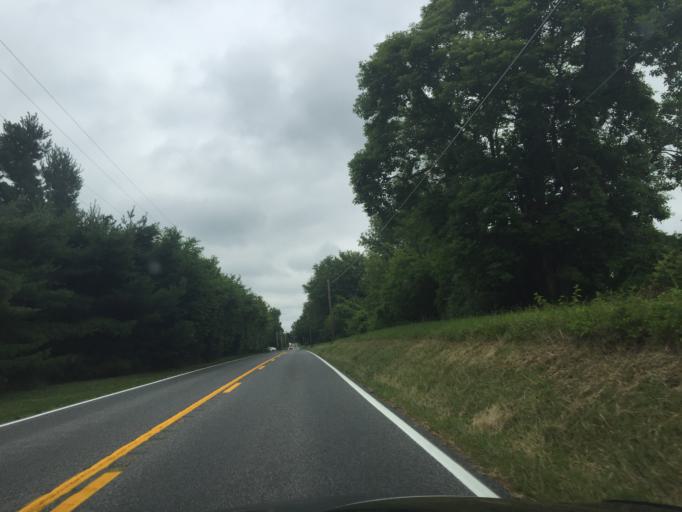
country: US
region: Maryland
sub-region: Harford County
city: Jarrettsville
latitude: 39.5731
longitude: -76.5191
